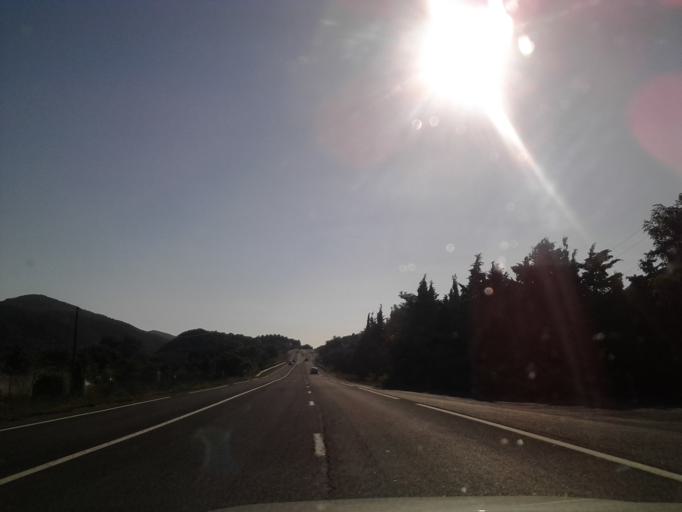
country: FR
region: Languedoc-Roussillon
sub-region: Departement des Pyrenees-Orientales
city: Vinca
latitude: 42.6446
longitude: 2.5065
